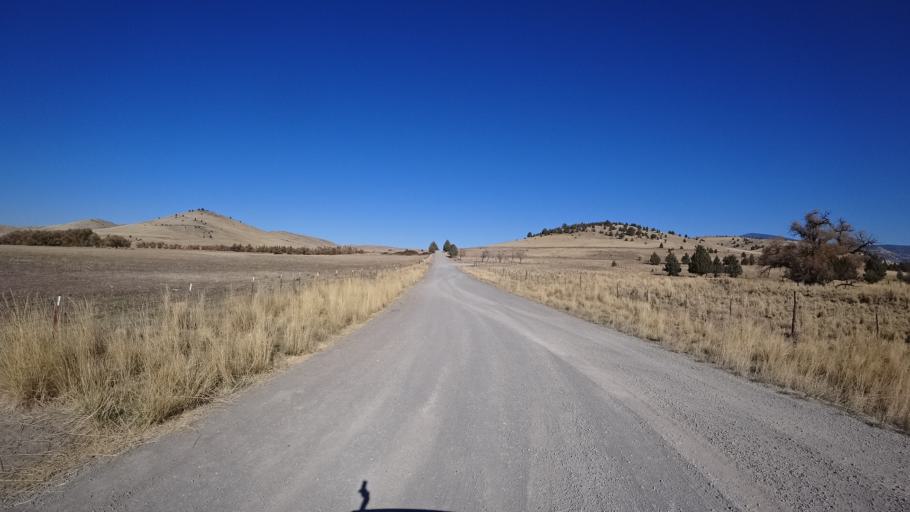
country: US
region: California
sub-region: Siskiyou County
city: Montague
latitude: 41.7265
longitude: -122.3696
